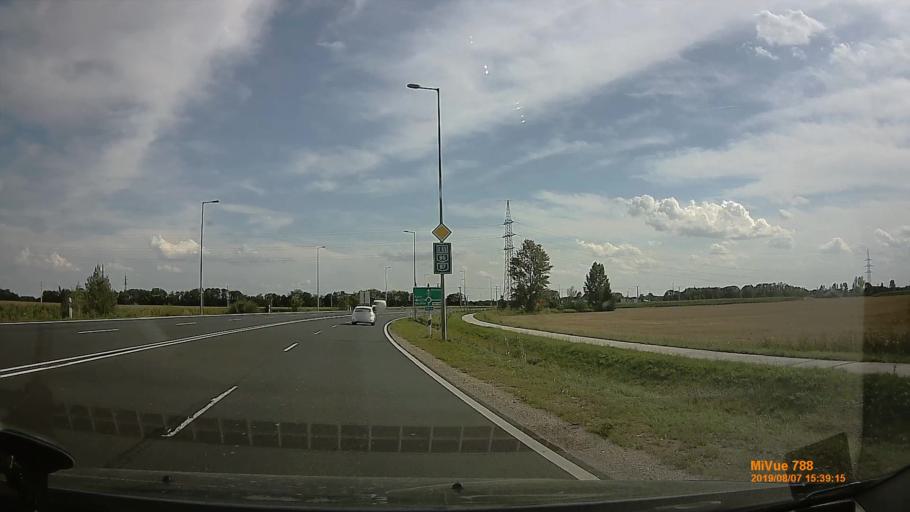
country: HU
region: Vas
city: Szombathely
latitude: 47.2239
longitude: 16.6583
